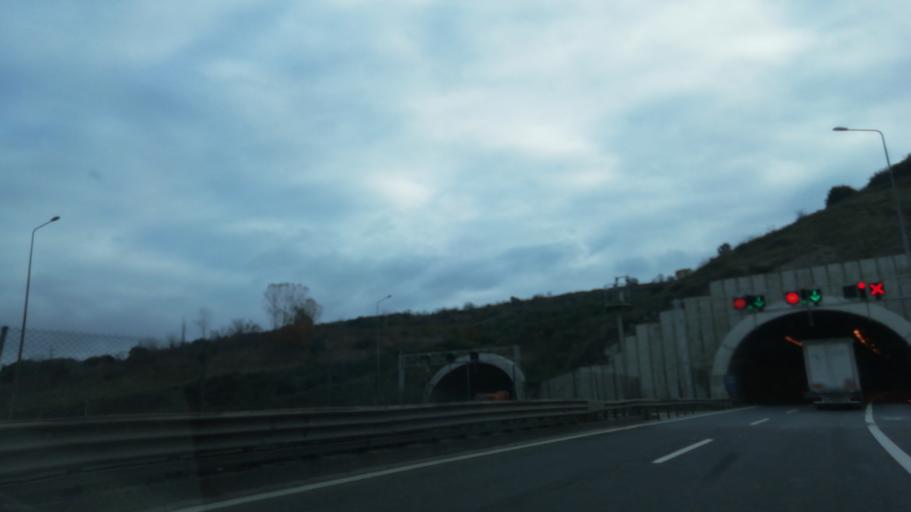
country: TR
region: Kocaeli
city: Izmit
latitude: 40.7788
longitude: 29.8875
